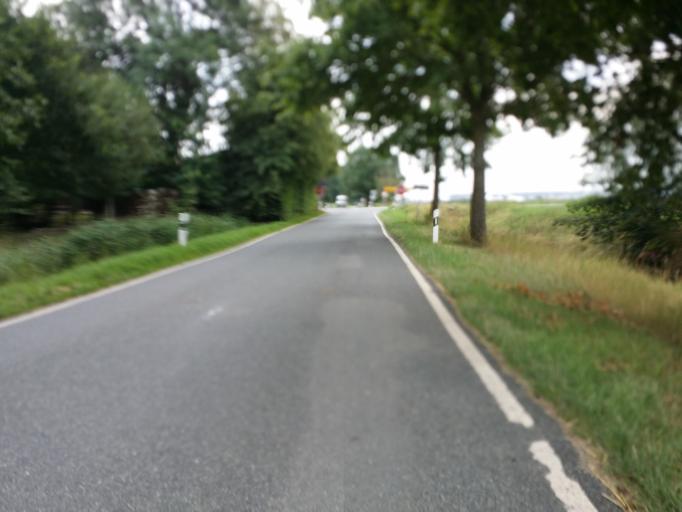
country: DE
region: Schleswig-Holstein
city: Bahrenfleth
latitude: 53.8764
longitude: 9.4596
